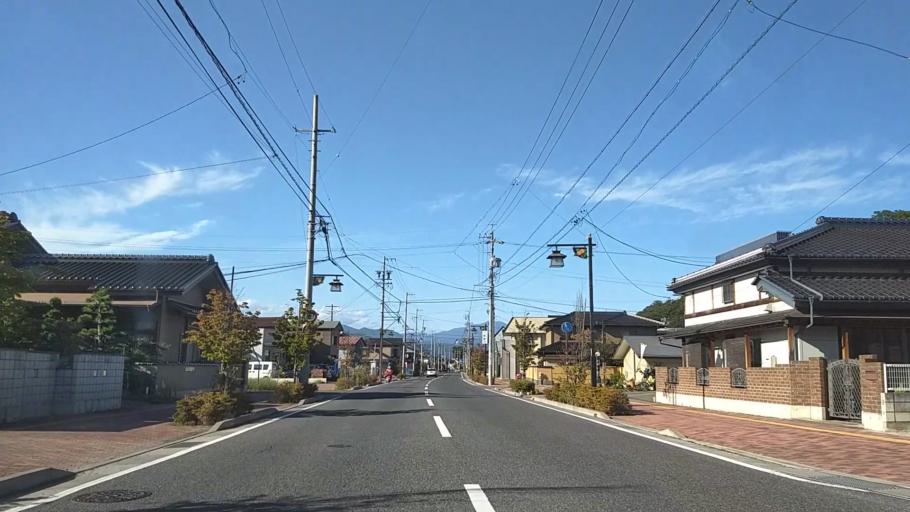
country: JP
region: Nagano
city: Nagano-shi
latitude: 36.5329
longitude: 138.1266
